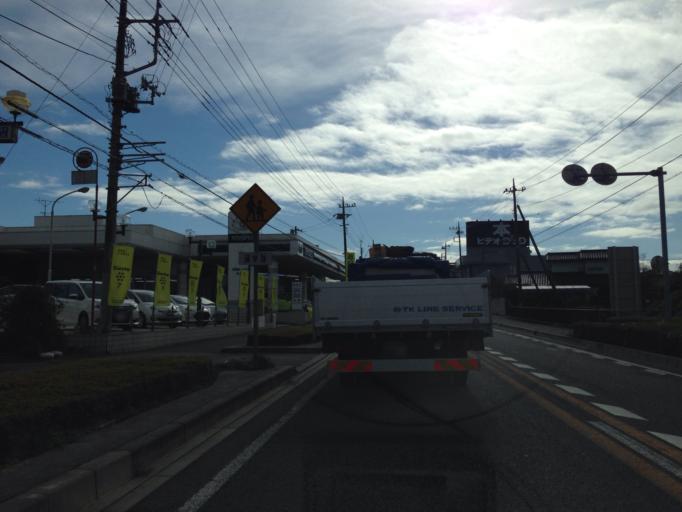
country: JP
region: Ibaraki
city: Ushiku
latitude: 35.9674
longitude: 140.1396
